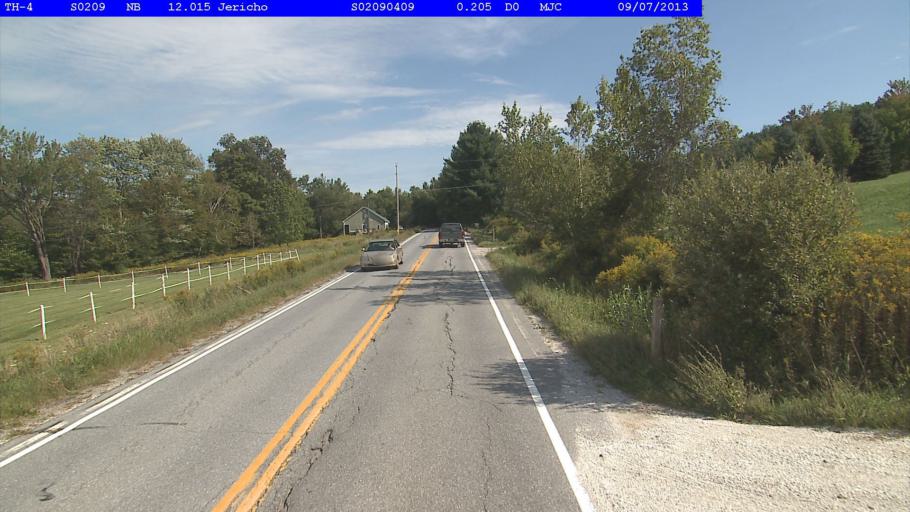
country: US
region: Vermont
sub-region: Chittenden County
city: Jericho
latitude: 44.4344
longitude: -72.9804
